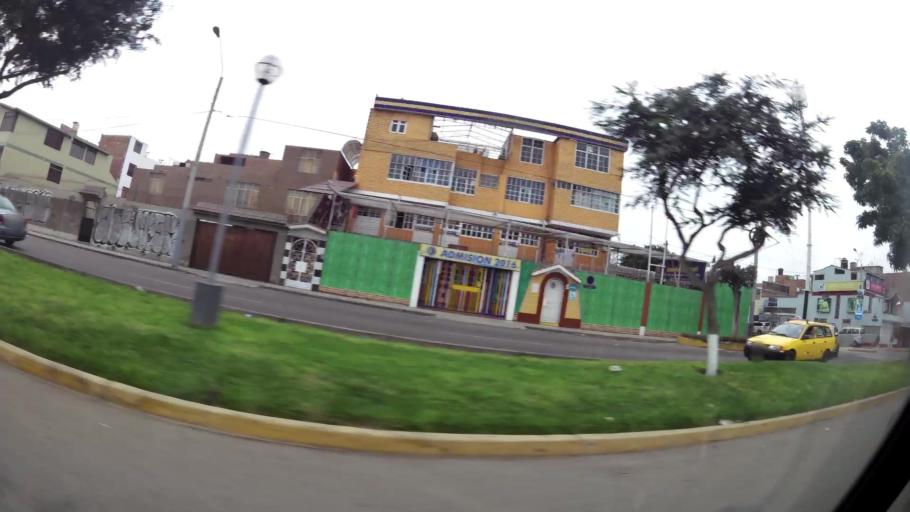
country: PE
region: Callao
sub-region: Callao
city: Callao
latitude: -12.0644
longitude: -77.1045
